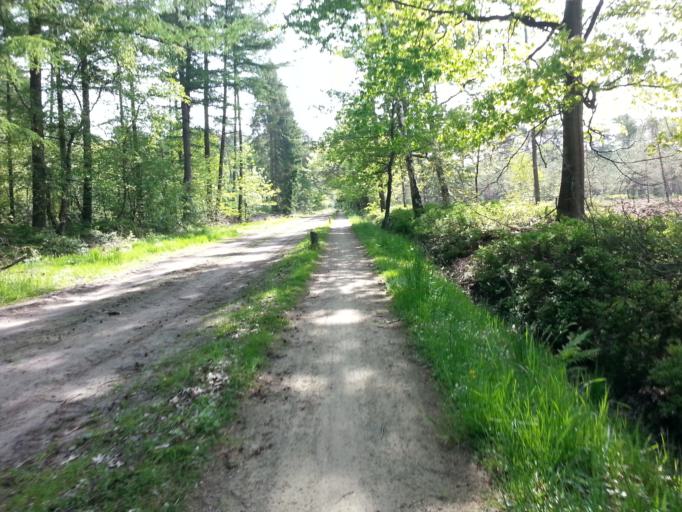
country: NL
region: Overijssel
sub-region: Gemeente Haaksbergen
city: Haaksbergen
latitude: 52.1309
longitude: 6.6964
